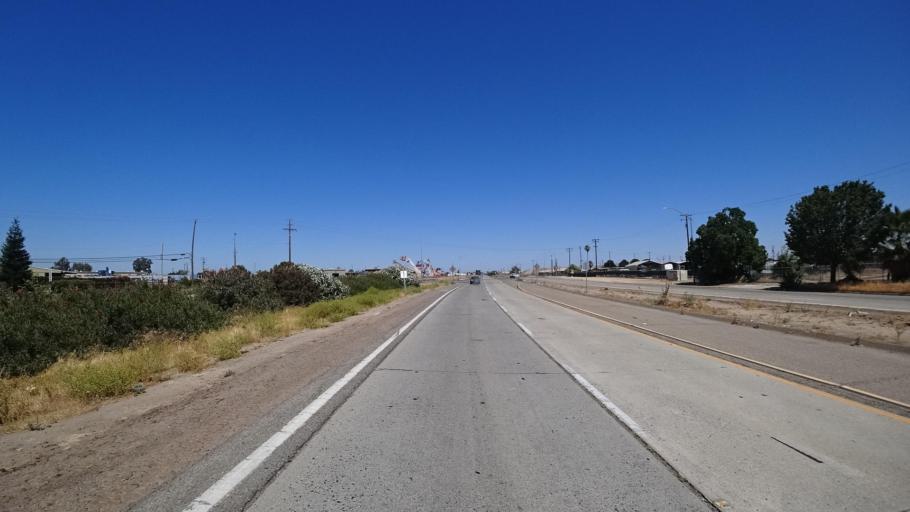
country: US
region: California
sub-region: Fresno County
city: Fresno
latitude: 36.7011
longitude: -119.7629
